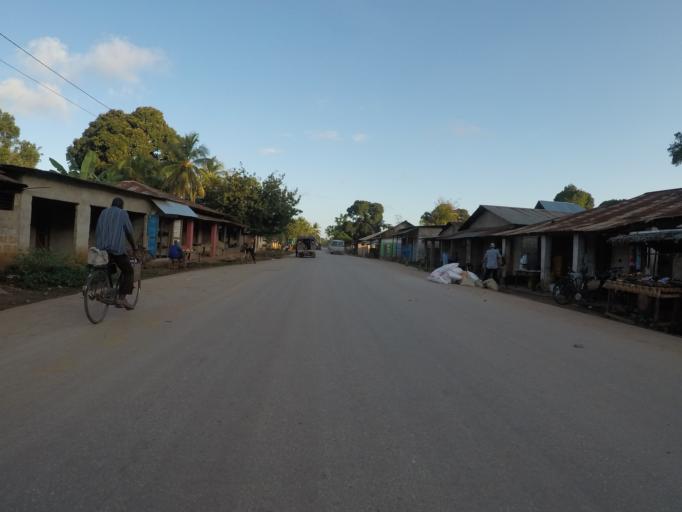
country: TZ
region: Zanzibar North
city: Gamba
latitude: -5.8869
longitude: 39.2873
